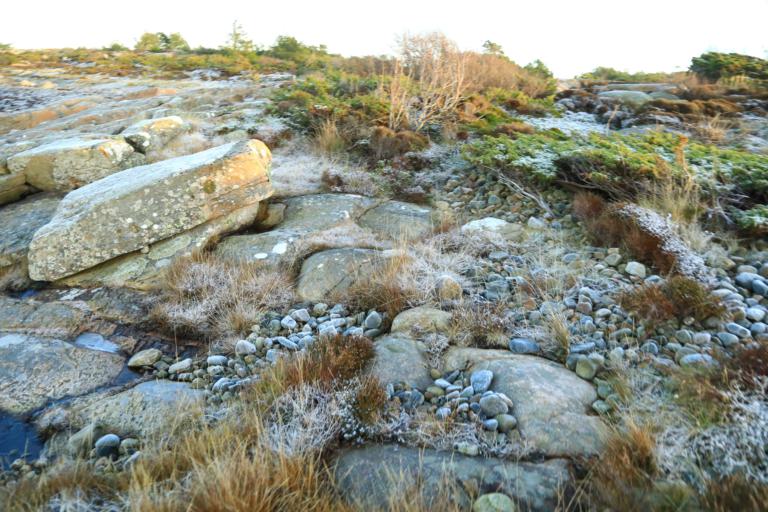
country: SE
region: Halland
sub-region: Kungsbacka Kommun
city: Frillesas
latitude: 57.1972
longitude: 12.1620
